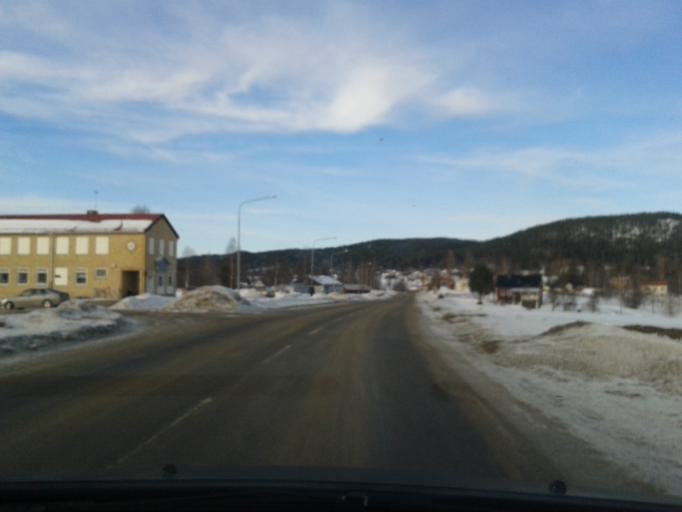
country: SE
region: Vaesternorrland
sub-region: OErnskoeldsviks Kommun
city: Bredbyn
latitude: 63.5123
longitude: 18.0643
